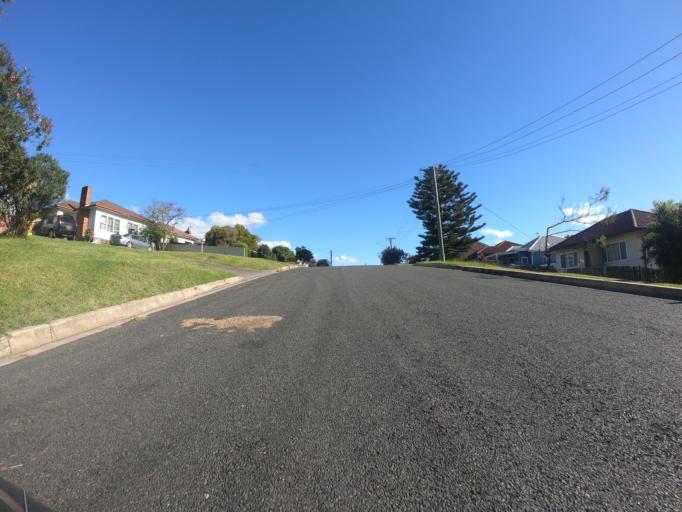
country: AU
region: New South Wales
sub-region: Wollongong
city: Port Kembla
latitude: -34.4809
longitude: 150.8910
